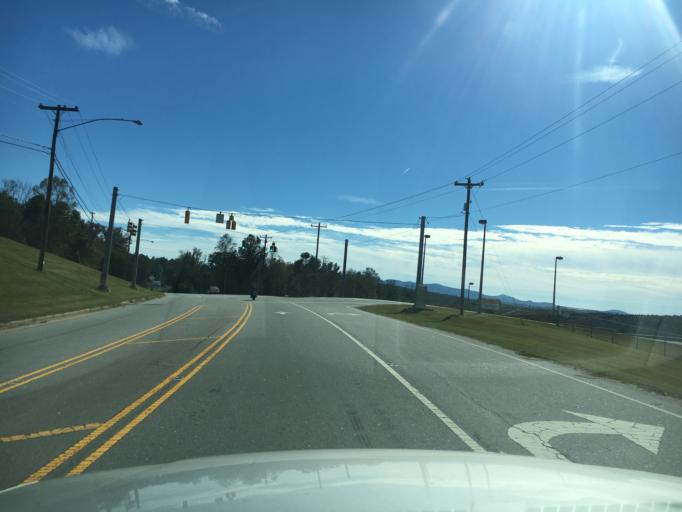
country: US
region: North Carolina
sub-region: Burke County
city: Morganton
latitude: 35.7817
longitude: -81.6895
